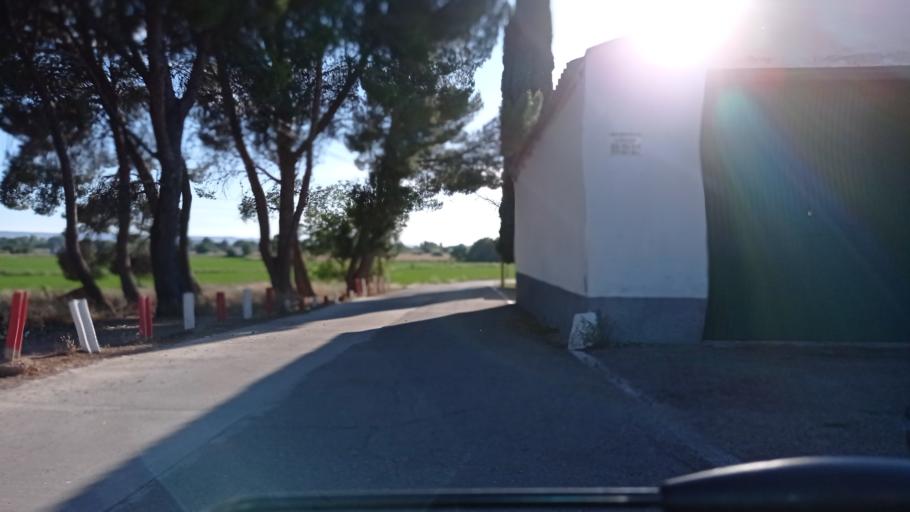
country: ES
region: Aragon
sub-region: Provincia de Zaragoza
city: Oliver-Valdefierro, Oliver, Valdefierro
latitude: 41.6641
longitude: -0.9549
